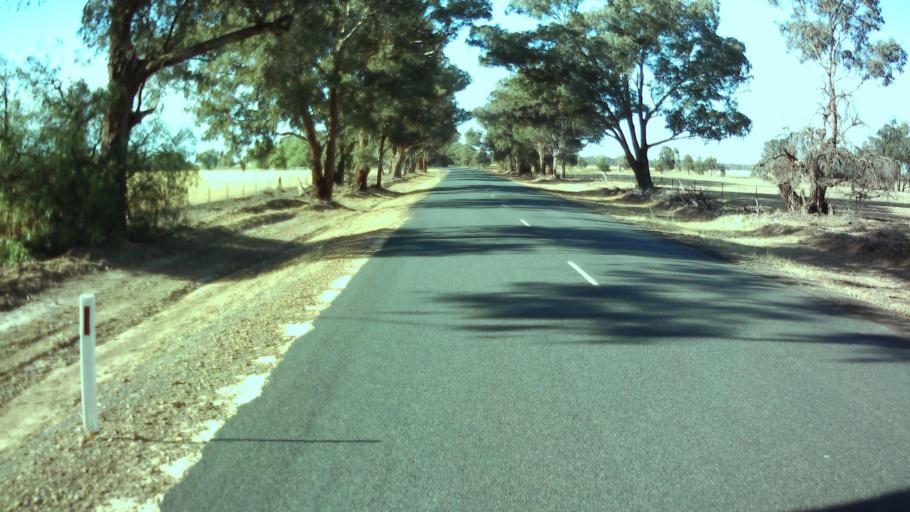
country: AU
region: New South Wales
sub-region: Weddin
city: Grenfell
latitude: -33.9777
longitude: 148.1410
